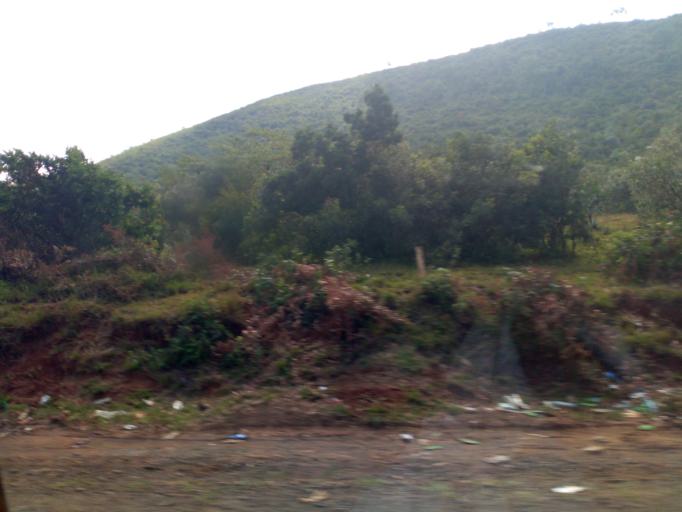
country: KE
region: Nakuru
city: Kijabe
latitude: -1.0169
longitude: 36.6012
